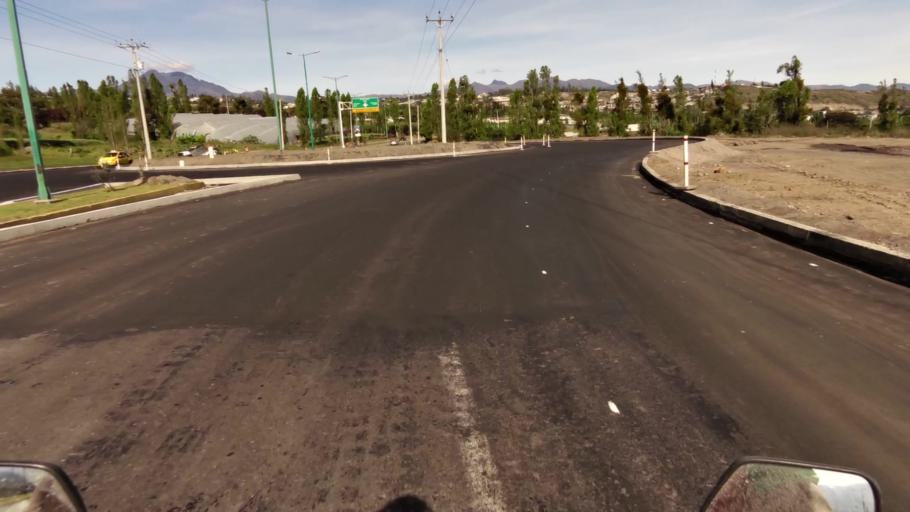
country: EC
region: Imbabura
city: Ibarra
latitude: 0.3331
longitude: -78.1555
